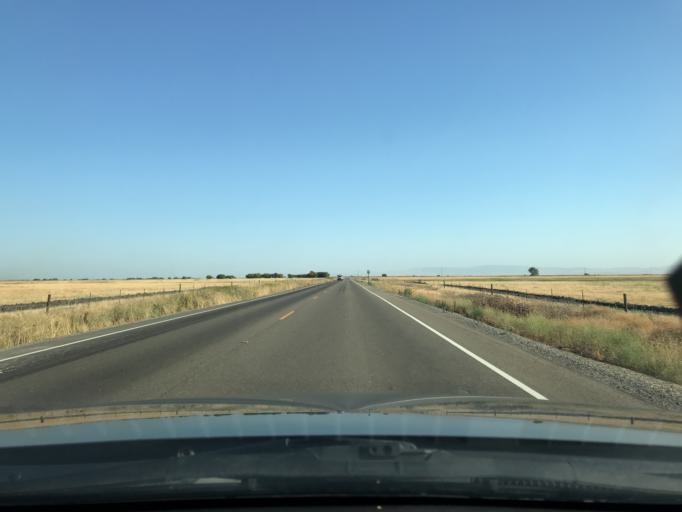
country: US
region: California
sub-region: Merced County
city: Gustine
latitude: 37.2246
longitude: -120.8521
